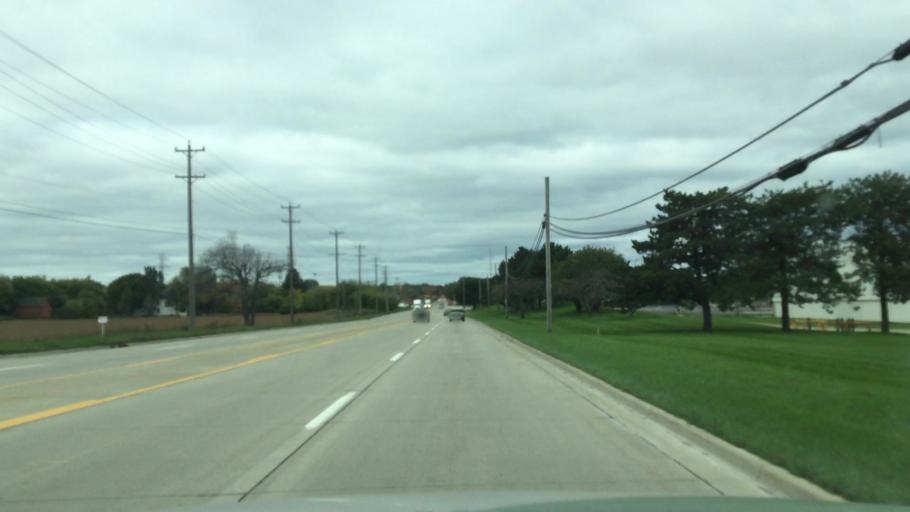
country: US
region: Michigan
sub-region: Macomb County
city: Romeo
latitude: 42.8032
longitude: -82.9944
